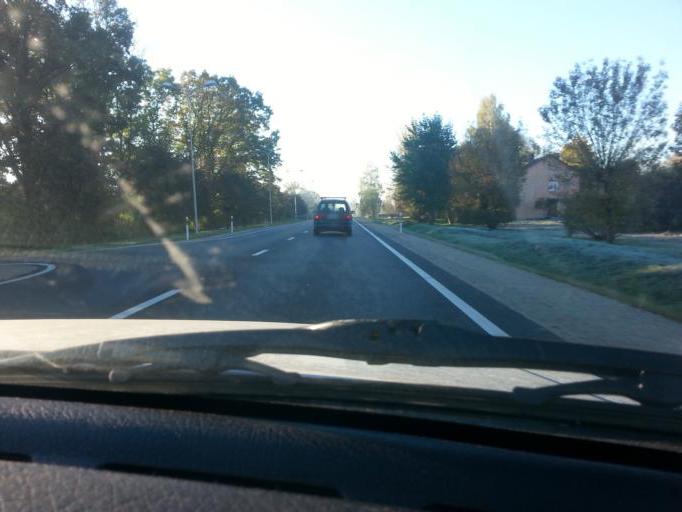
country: LT
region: Siauliu apskritis
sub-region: Joniskis
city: Joniskis
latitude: 56.4130
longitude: 23.6829
